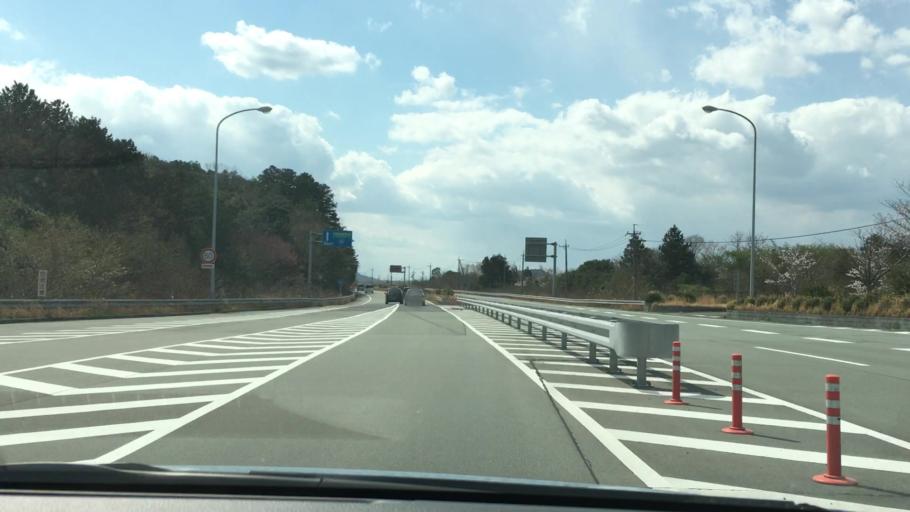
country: JP
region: Mie
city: Toba
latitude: 34.4944
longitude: 136.7773
